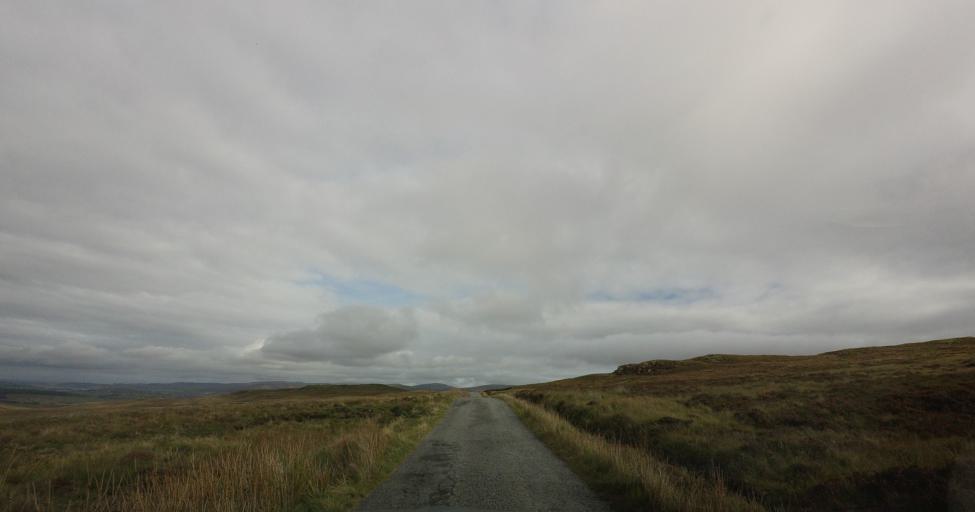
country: GB
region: Scotland
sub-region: Highland
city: Isle of Skye
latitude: 57.4045
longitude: -6.2672
